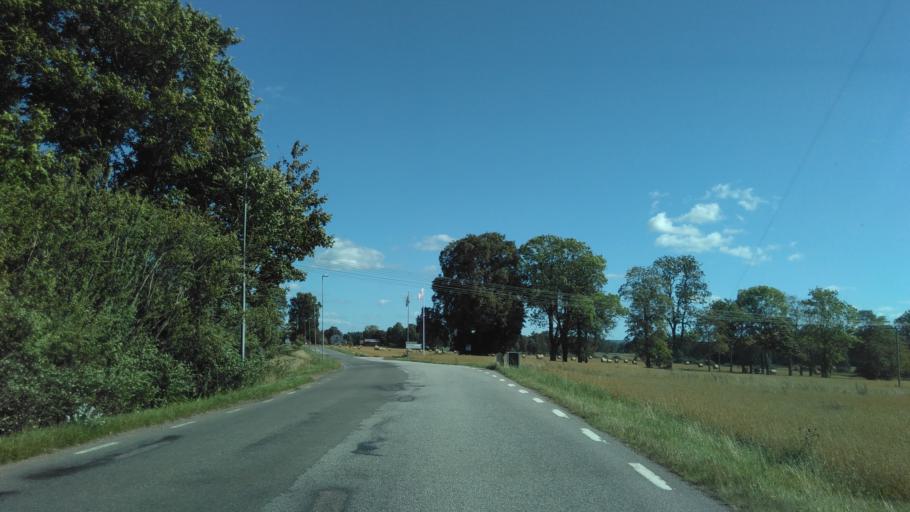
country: SE
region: Vaestra Goetaland
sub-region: Skara Kommun
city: Skara
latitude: 58.3841
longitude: 13.4725
